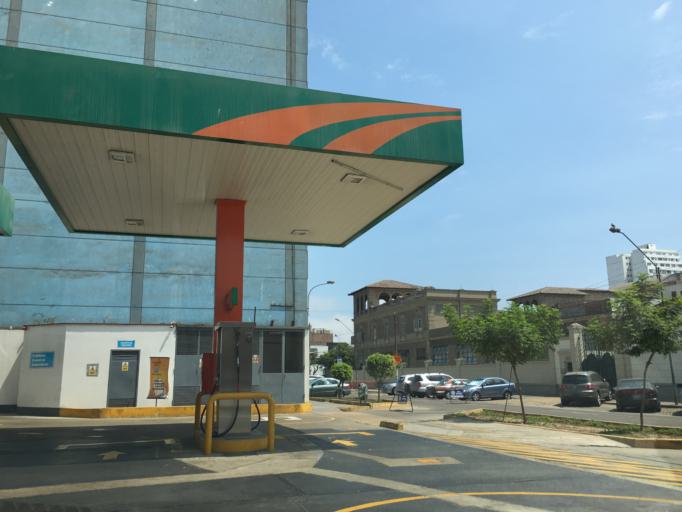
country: PE
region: Lima
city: Lima
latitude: -12.0756
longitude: -77.0347
